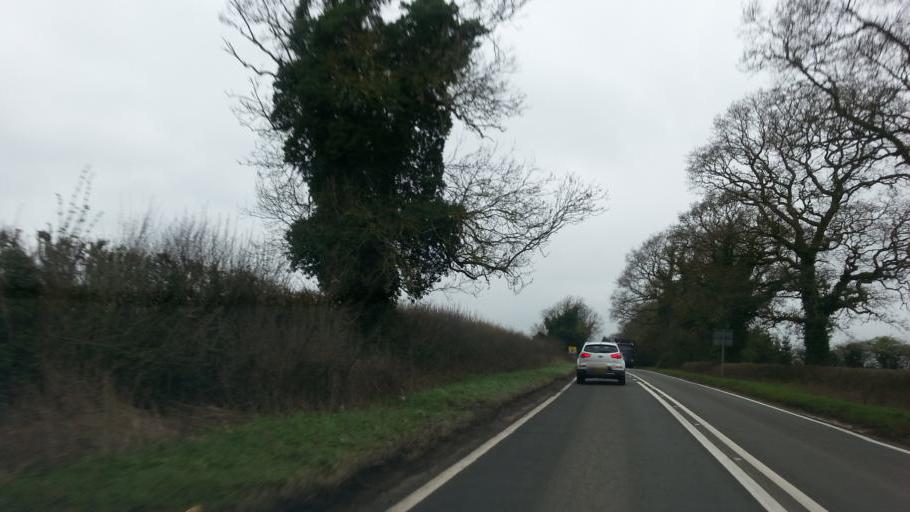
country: GB
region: England
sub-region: Oxfordshire
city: Adderbury
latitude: 52.0609
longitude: -1.2410
